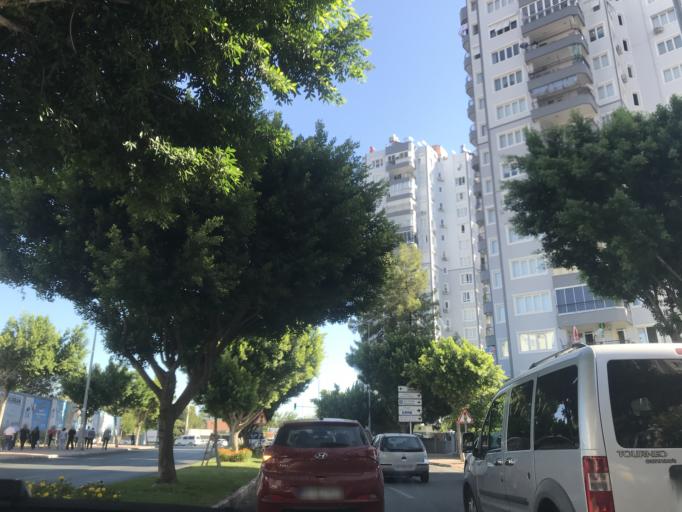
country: TR
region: Antalya
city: Antalya
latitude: 36.8988
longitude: 30.6305
